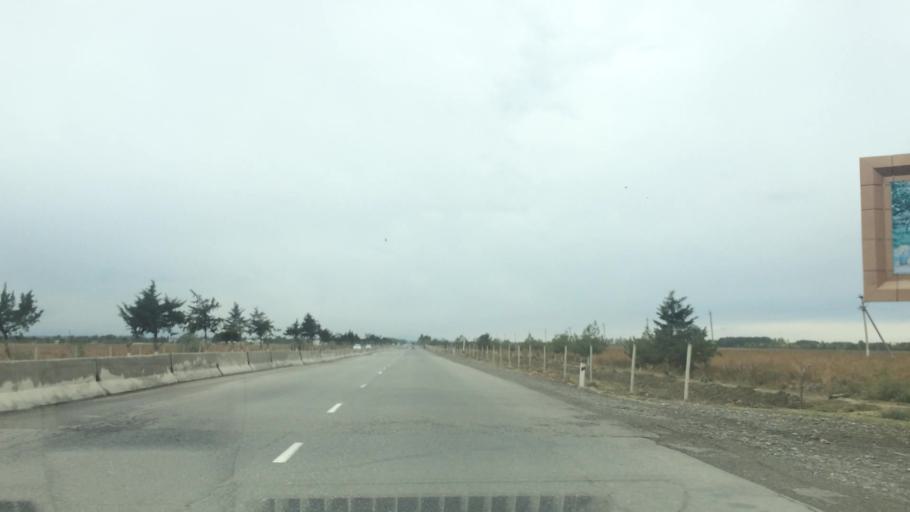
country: UZ
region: Samarqand
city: Bulung'ur
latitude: 39.7934
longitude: 67.3252
